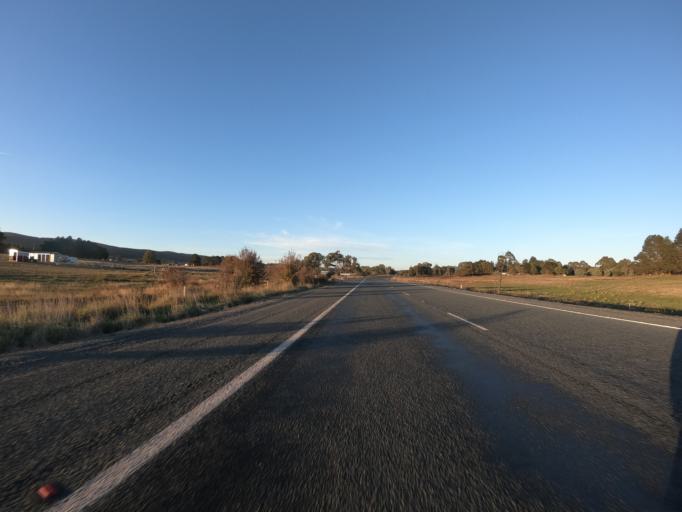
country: AU
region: New South Wales
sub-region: Goulburn Mulwaree
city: Goulburn
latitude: -34.8248
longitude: 149.5983
